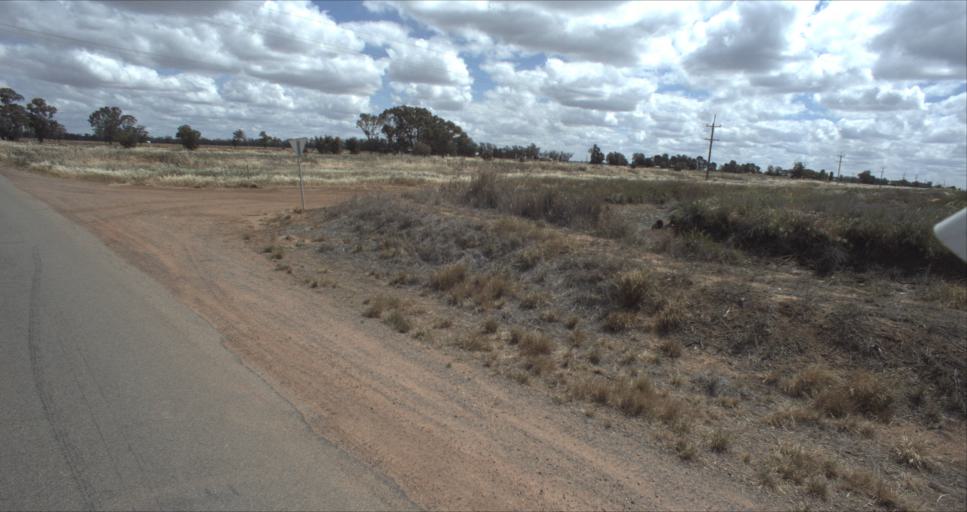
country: AU
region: New South Wales
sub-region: Leeton
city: Leeton
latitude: -34.5897
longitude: 146.3698
